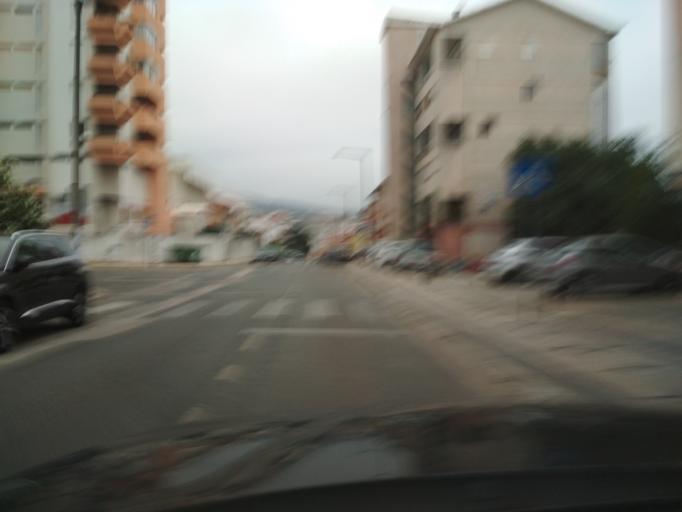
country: PT
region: Coimbra
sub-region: Coimbra
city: Coimbra
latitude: 40.1971
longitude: -8.4110
